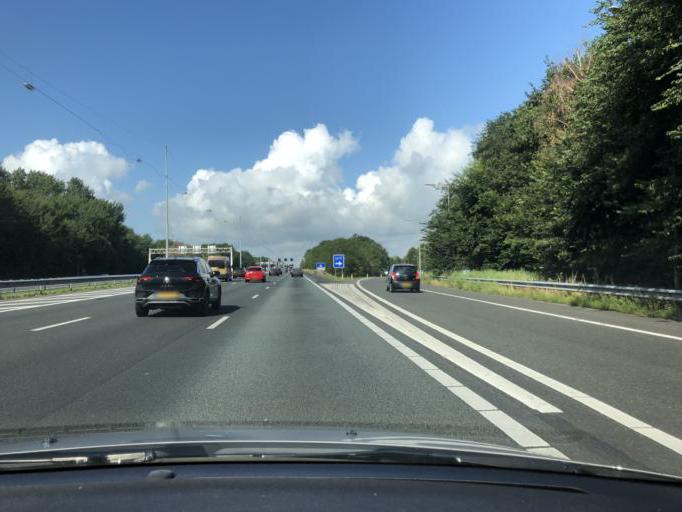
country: NL
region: North Holland
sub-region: Gemeente Naarden
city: Naarden
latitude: 52.3063
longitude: 5.1496
